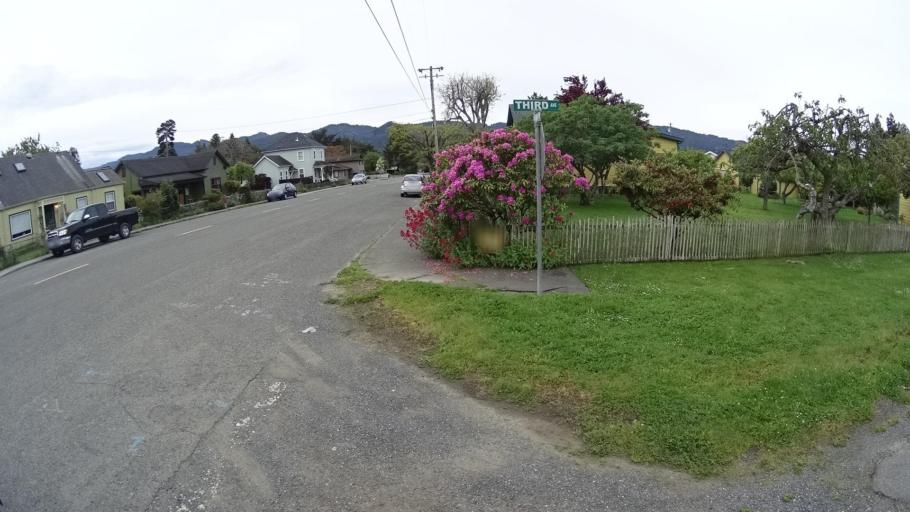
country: US
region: California
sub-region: Humboldt County
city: Blue Lake
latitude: 40.8816
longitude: -123.9864
